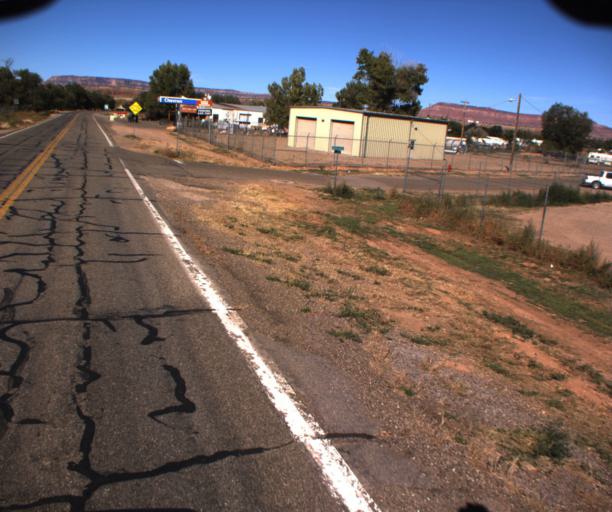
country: US
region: Arizona
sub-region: Coconino County
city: Fredonia
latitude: 36.9392
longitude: -112.5201
